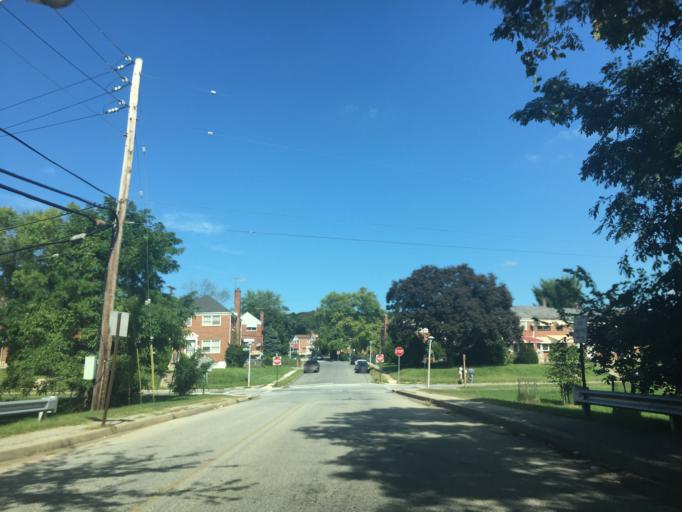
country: US
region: Maryland
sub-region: Baltimore County
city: Rosedale
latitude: 39.3235
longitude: -76.5614
